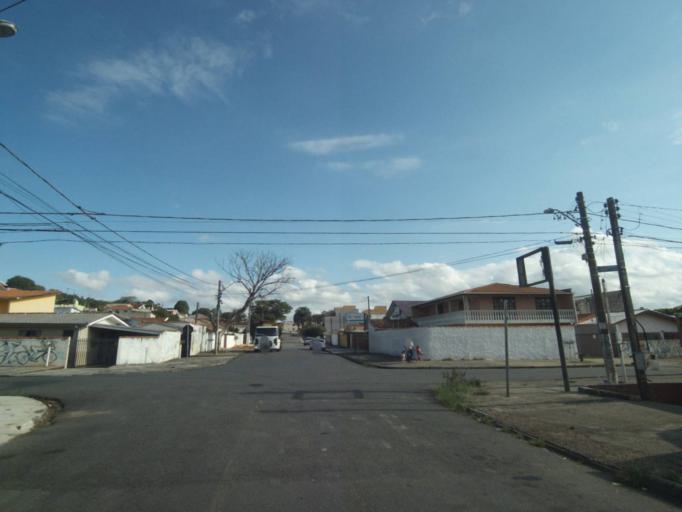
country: BR
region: Parana
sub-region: Curitiba
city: Curitiba
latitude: -25.3889
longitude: -49.3028
